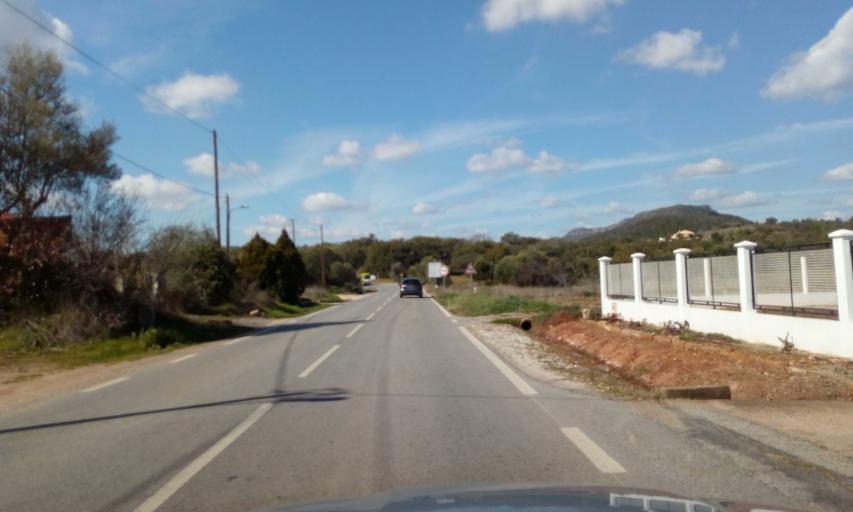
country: PT
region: Faro
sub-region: Loule
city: Loule
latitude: 37.2442
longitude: -8.0577
